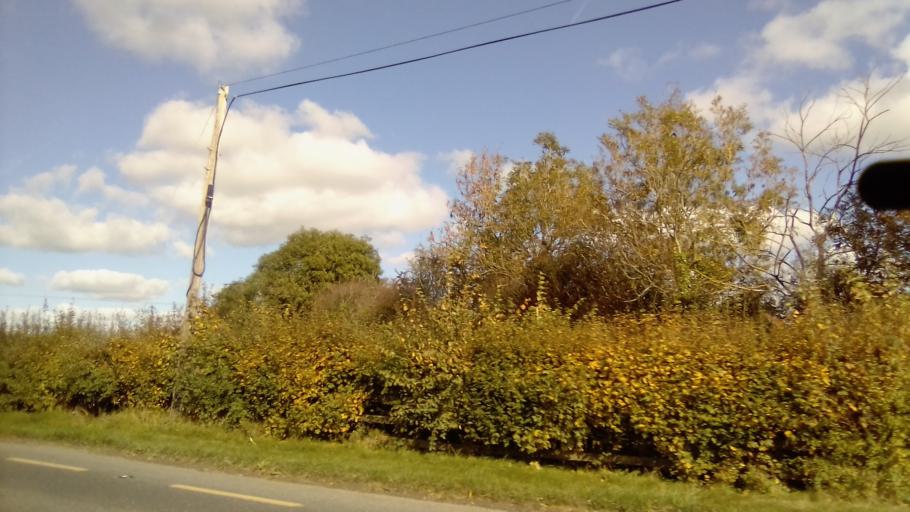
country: IE
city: Kentstown
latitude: 53.6480
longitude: -6.5106
